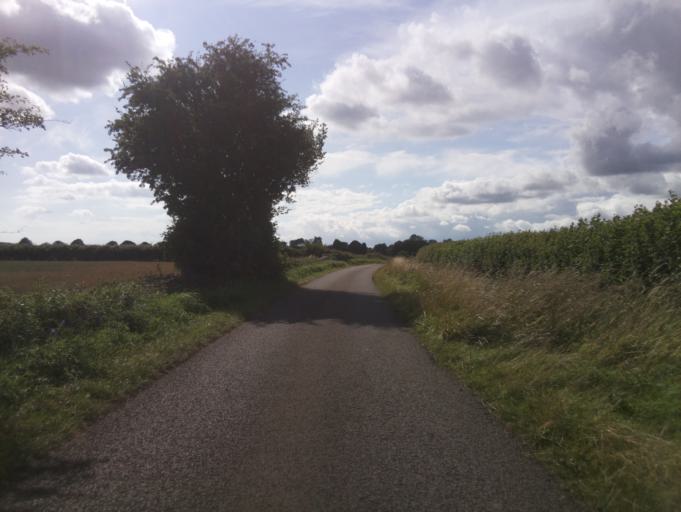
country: GB
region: England
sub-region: Gloucestershire
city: Coates
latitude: 51.6956
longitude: -2.0955
